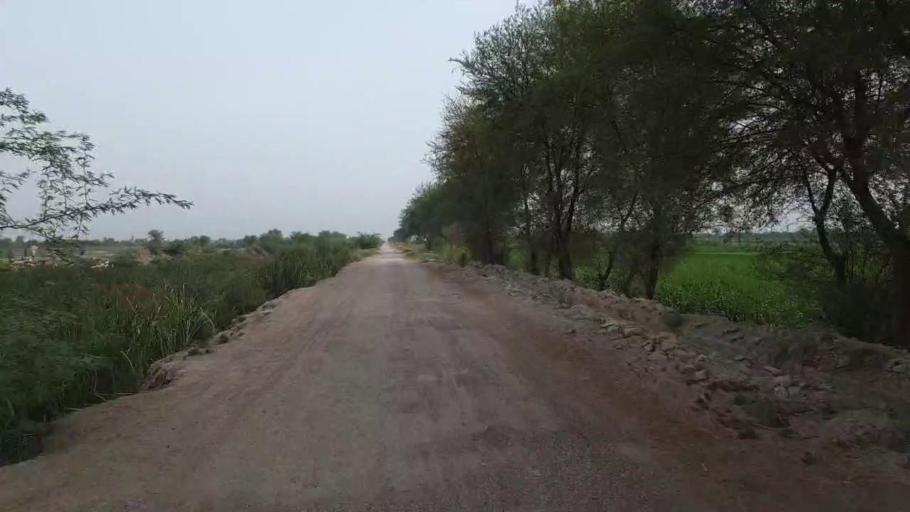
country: PK
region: Sindh
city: Daur
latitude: 26.4236
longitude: 68.2251
